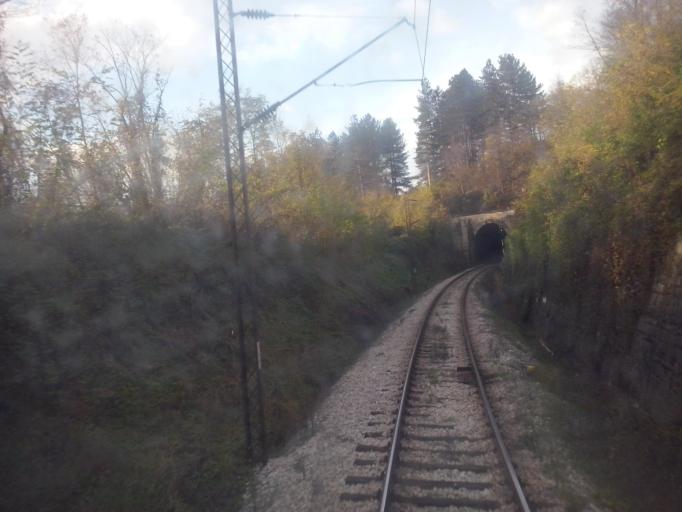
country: RS
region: Central Serbia
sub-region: Zlatiborski Okrug
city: Kosjeric
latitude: 43.9934
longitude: 19.9180
